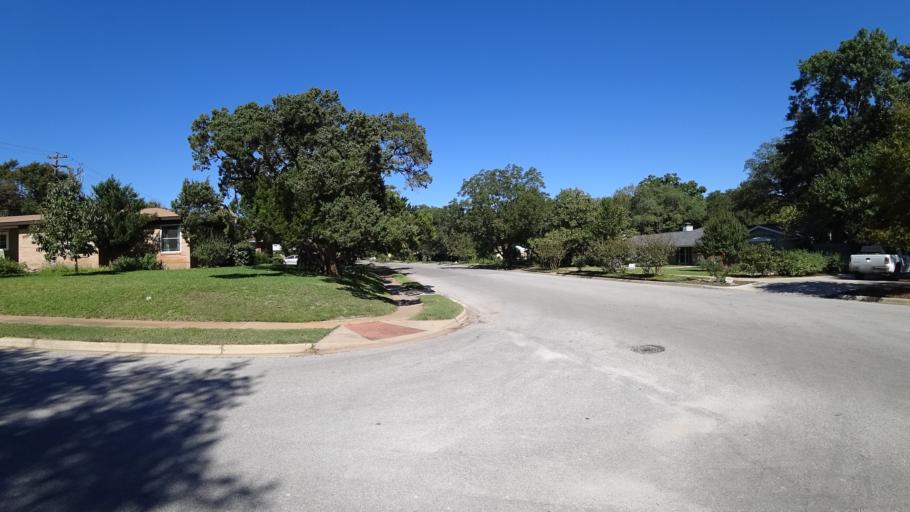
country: US
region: Texas
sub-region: Travis County
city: West Lake Hills
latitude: 30.3376
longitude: -97.7493
